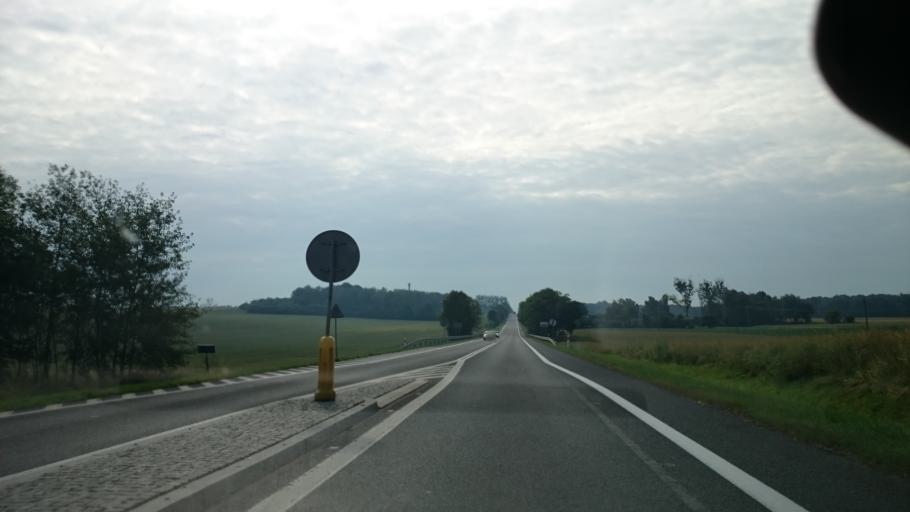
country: PL
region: Opole Voivodeship
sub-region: Powiat strzelecki
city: Jemielnica
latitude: 50.4879
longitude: 18.4158
